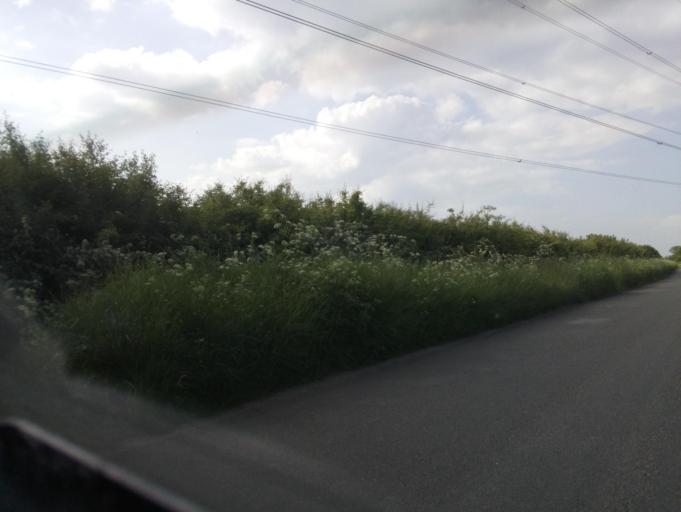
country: GB
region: England
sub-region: Wiltshire
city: Bremhill
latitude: 51.4989
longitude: -2.0737
